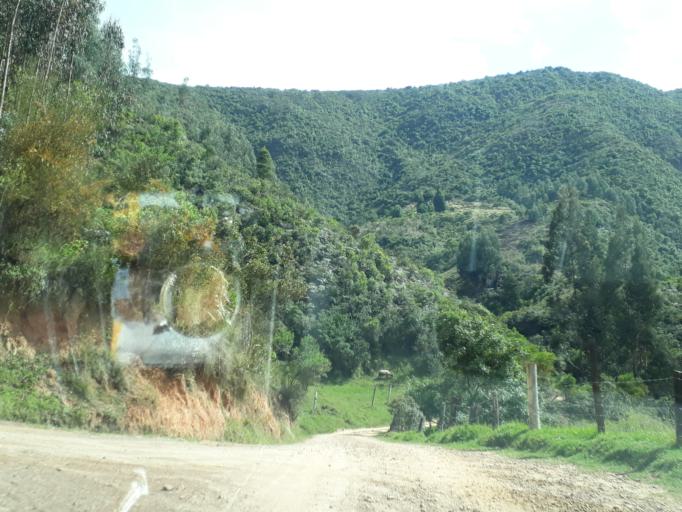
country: CO
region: Boyaca
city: Santa Rosa de Viterbo
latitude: 5.8524
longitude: -72.9640
